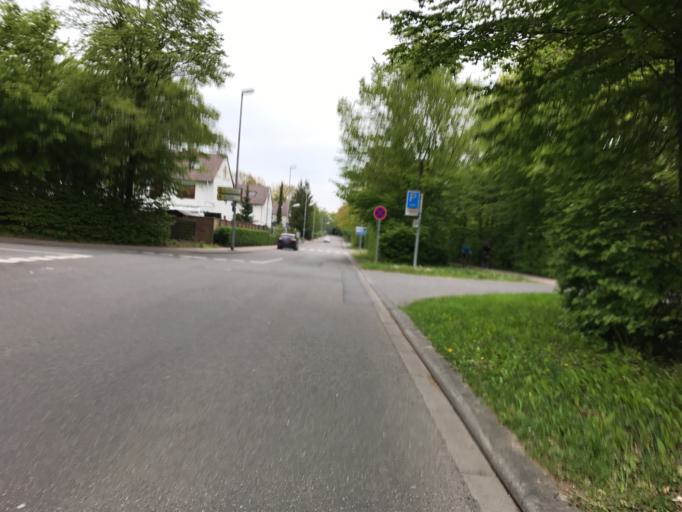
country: DE
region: Rheinland-Pfalz
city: Ober-Olm
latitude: 49.9565
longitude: 8.1896
